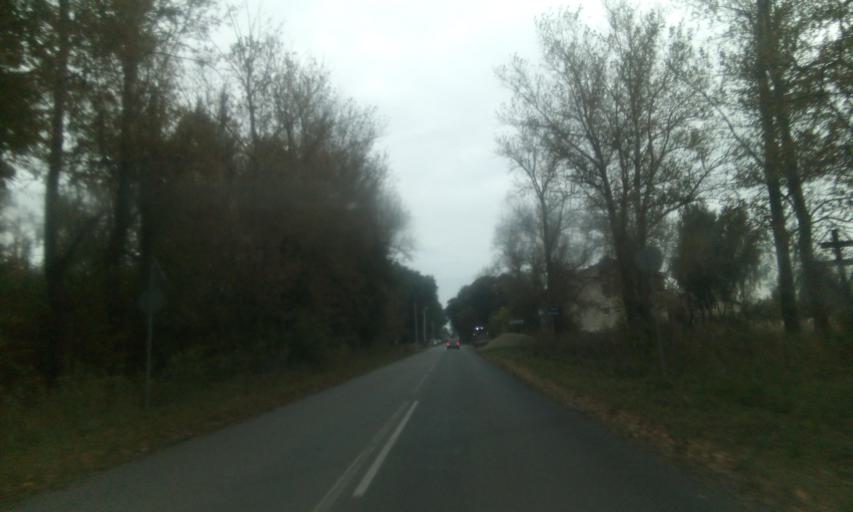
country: RU
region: Tula
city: Partizan
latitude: 53.9543
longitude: 38.0964
